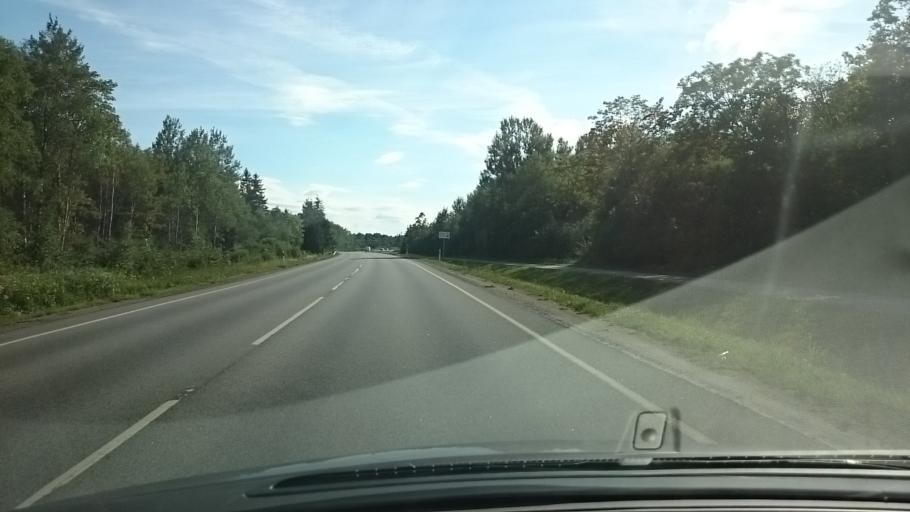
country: EE
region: Laeaene
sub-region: Ridala Parish
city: Uuemoisa
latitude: 58.9544
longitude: 23.6616
